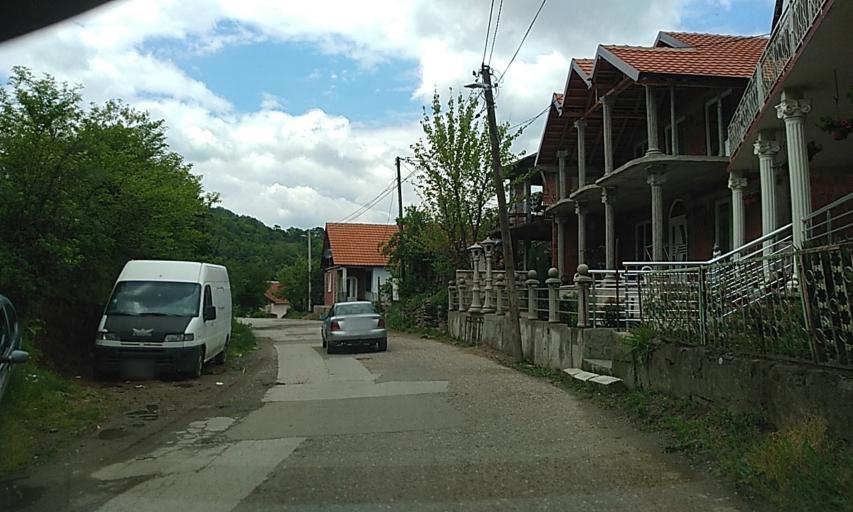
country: RS
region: Central Serbia
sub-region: Pcinjski Okrug
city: Vladicin Han
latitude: 42.7205
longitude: 22.0669
